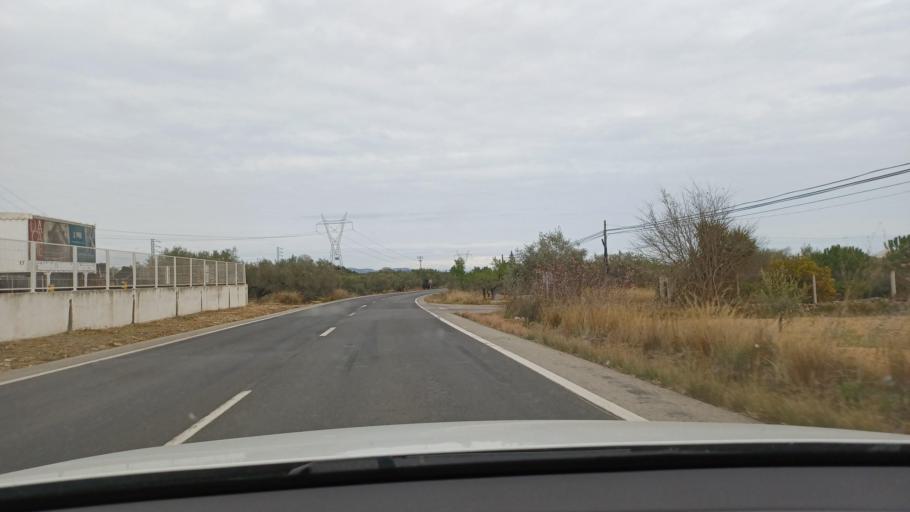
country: ES
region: Catalonia
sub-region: Provincia de Tarragona
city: Santa Barbara
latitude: 40.6892
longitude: 0.4715
